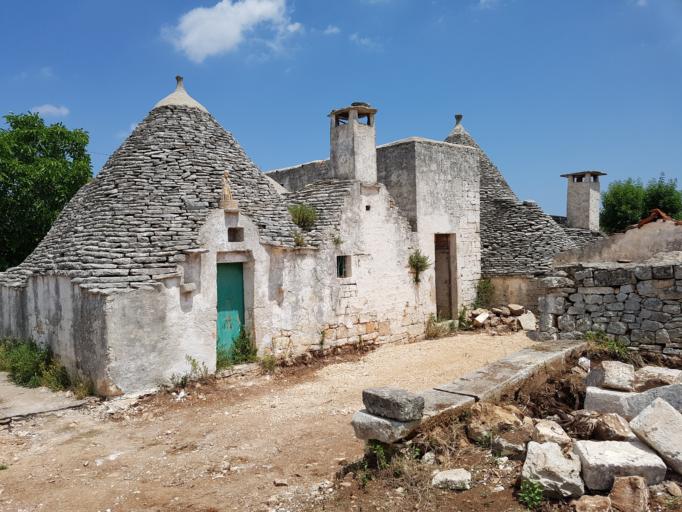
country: IT
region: Apulia
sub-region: Provincia di Bari
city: Alberobello
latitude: 40.7697
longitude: 17.2483
